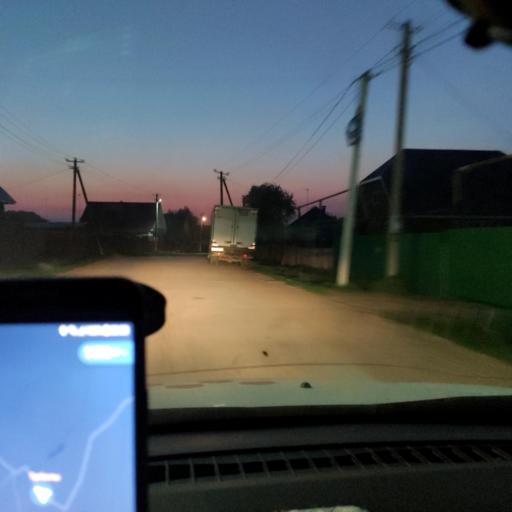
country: RU
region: Bashkortostan
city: Kabakovo
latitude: 54.6528
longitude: 56.3047
